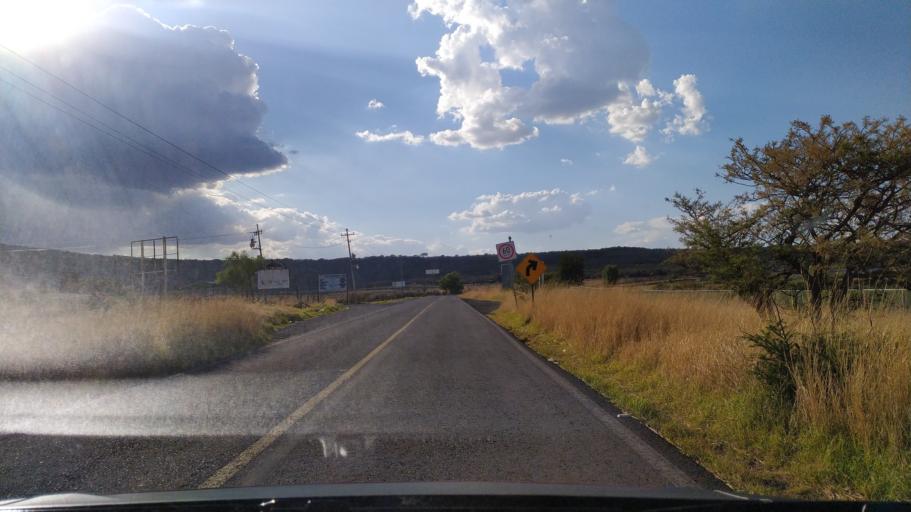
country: MX
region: Guanajuato
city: Ciudad Manuel Doblado
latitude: 20.5831
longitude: -101.9788
